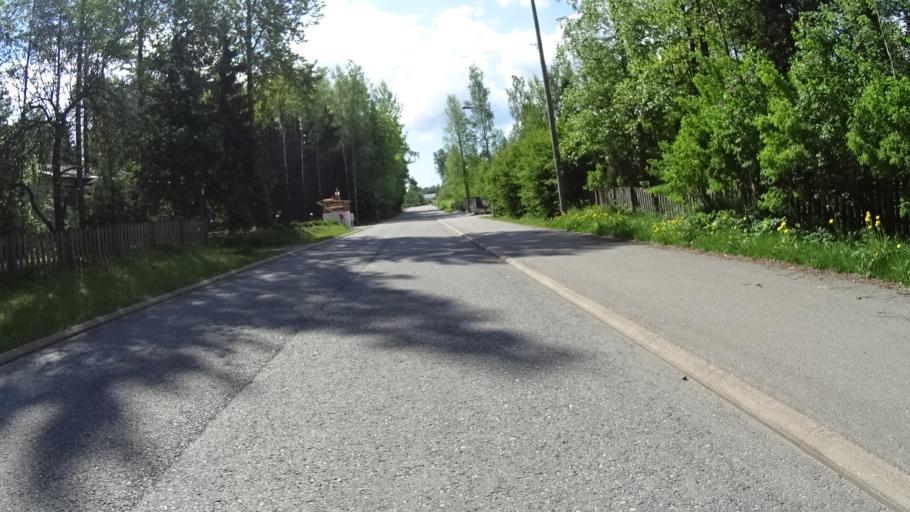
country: FI
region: Uusimaa
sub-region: Helsinki
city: Espoo
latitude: 60.2257
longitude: 24.6401
